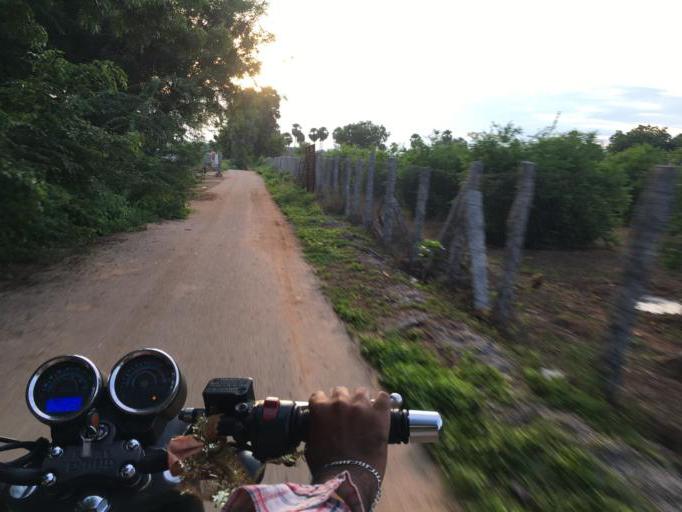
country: IN
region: Telangana
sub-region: Nalgonda
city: Nalgonda
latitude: 17.1758
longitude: 79.4157
